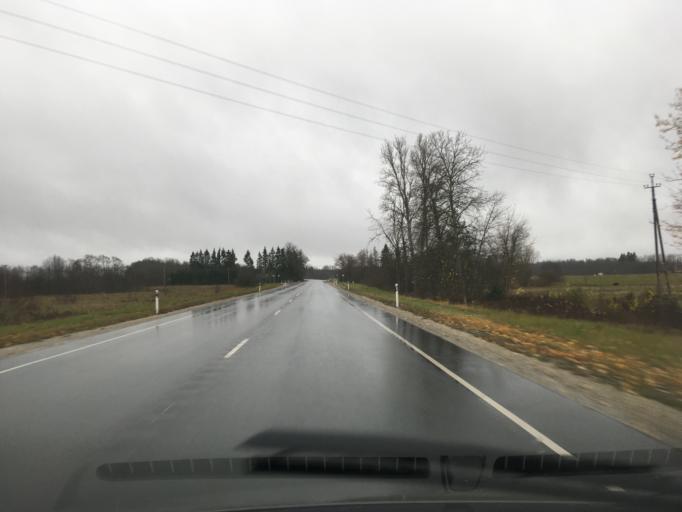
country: EE
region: Laeaene
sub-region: Lihula vald
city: Lihula
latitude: 58.8384
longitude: 24.0570
